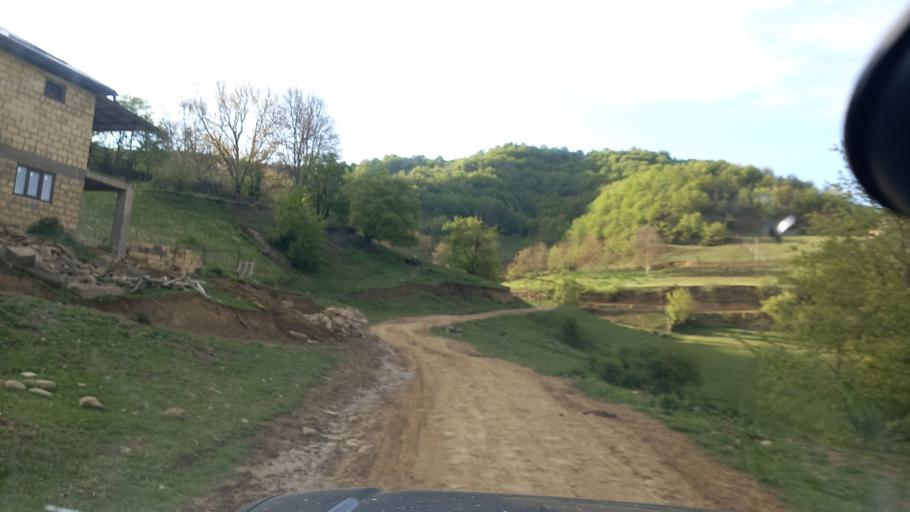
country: RU
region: Dagestan
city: Khuchni
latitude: 41.9465
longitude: 47.8342
